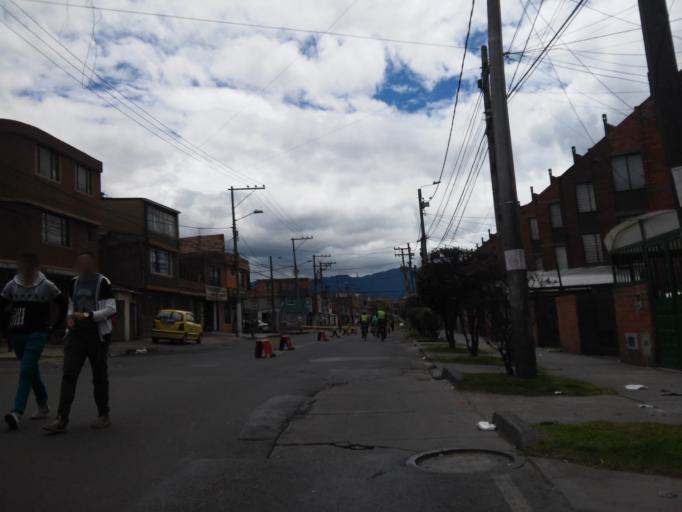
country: CO
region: Bogota D.C.
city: Bogota
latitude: 4.6089
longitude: -74.1467
